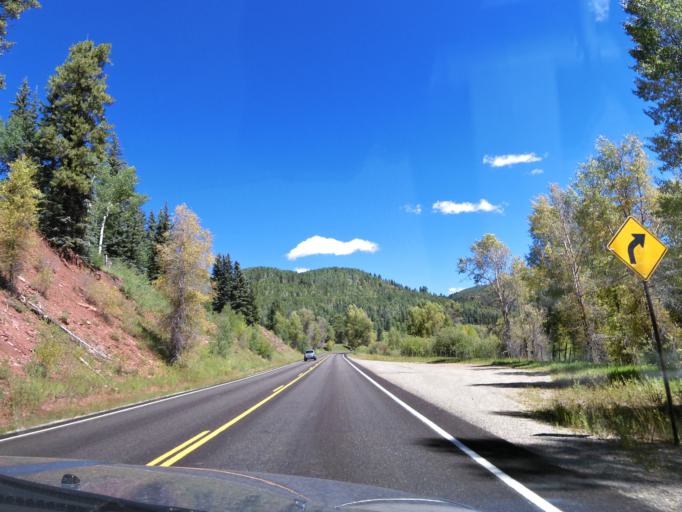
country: US
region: Colorado
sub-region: Montezuma County
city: Mancos
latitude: 37.6159
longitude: -108.0830
